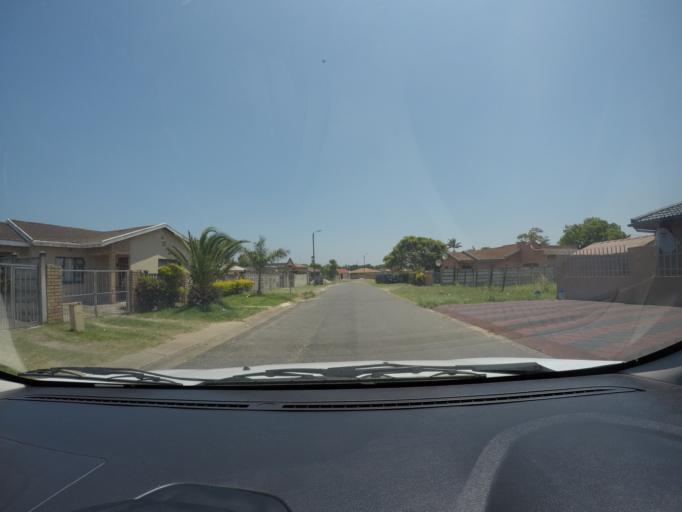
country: ZA
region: KwaZulu-Natal
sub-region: uThungulu District Municipality
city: eSikhawini
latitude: -28.8857
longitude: 31.8883
